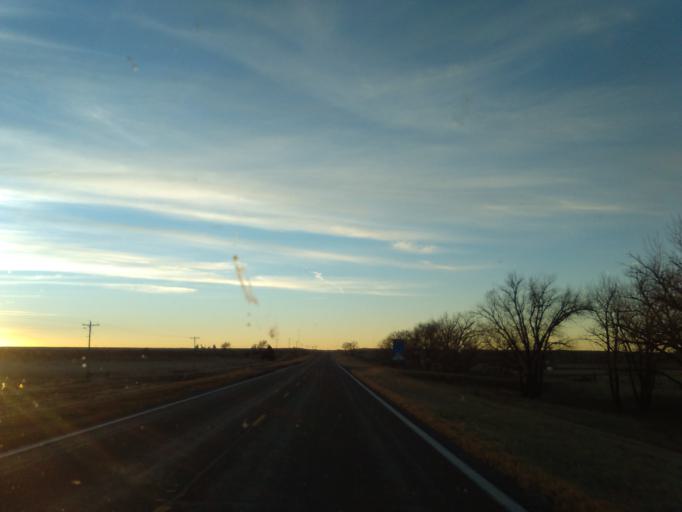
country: US
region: Kansas
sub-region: Wallace County
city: Sharon Springs
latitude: 38.9021
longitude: -101.6998
